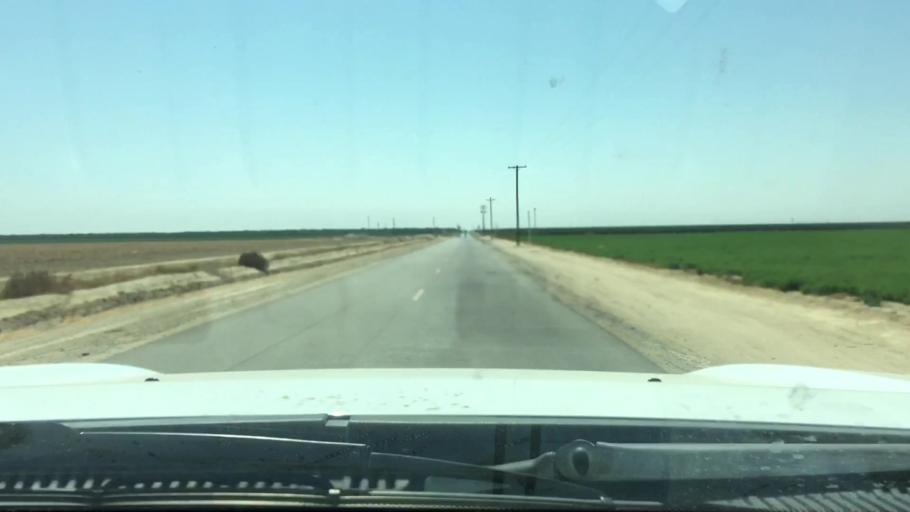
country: US
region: California
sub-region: Kern County
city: Wasco
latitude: 35.5851
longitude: -119.4026
